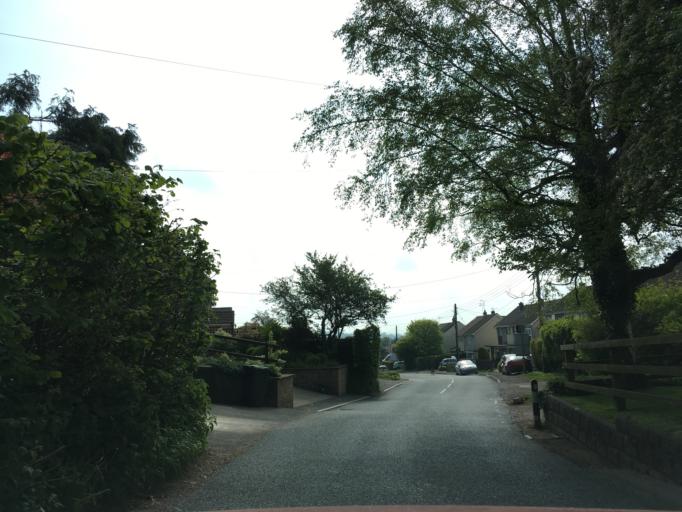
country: GB
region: England
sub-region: North Somerset
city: Winford
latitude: 51.3841
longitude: -2.6664
